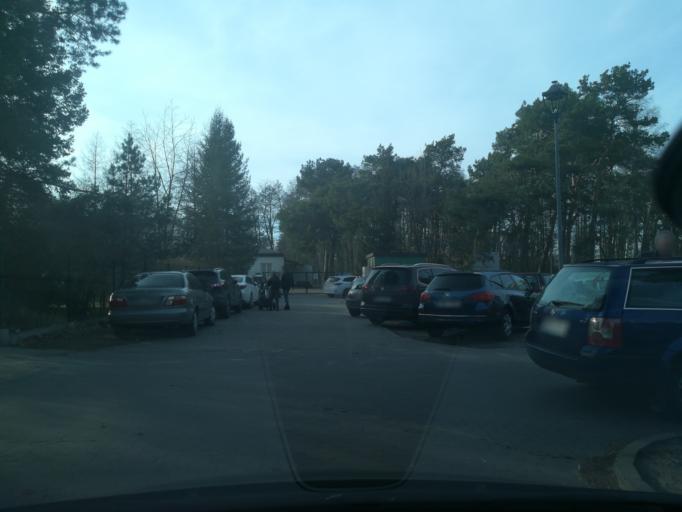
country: PL
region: Masovian Voivodeship
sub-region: Powiat piaseczynski
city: Konstancin-Jeziorna
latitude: 52.0853
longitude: 21.1096
